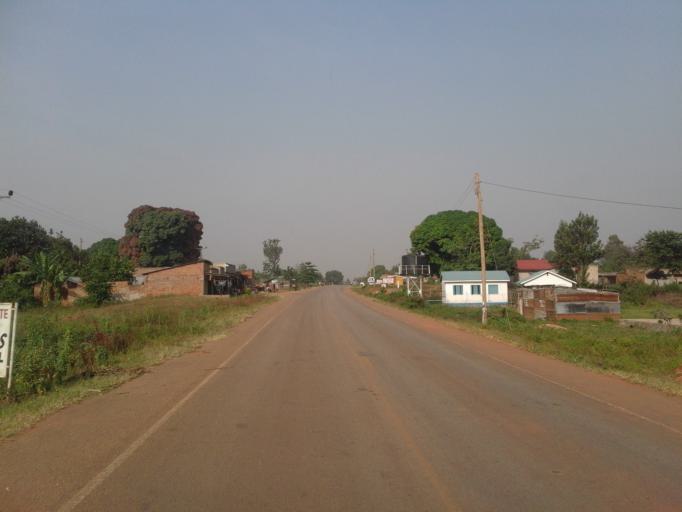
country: UG
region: Eastern Region
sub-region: Mbale District
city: Mbale
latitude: 1.0739
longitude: 34.1211
